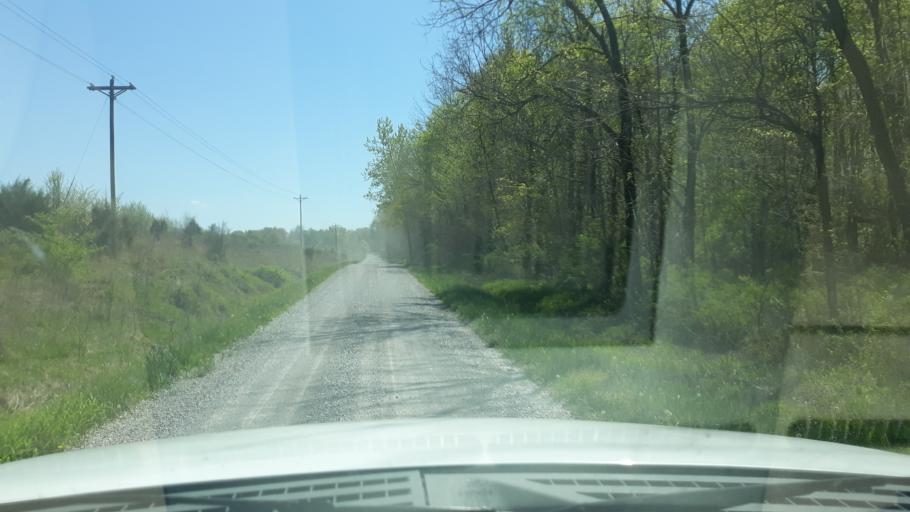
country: US
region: Illinois
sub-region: Saline County
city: Harrisburg
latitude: 37.8738
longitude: -88.6421
